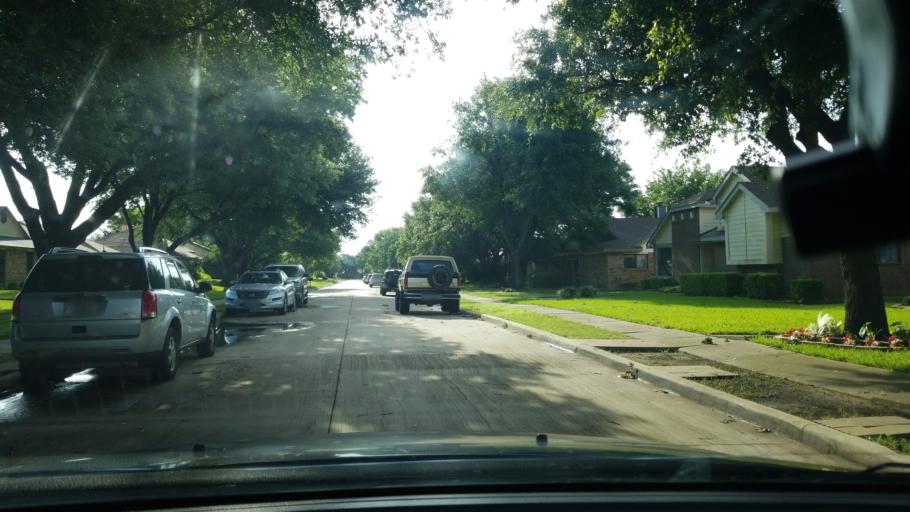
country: US
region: Texas
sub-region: Dallas County
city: Mesquite
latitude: 32.8045
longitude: -96.6089
